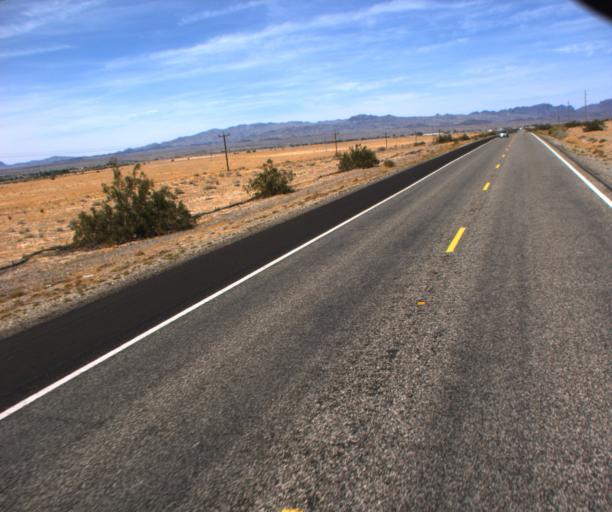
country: US
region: Arizona
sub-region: La Paz County
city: Parker
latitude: 34.1023
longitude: -114.2775
